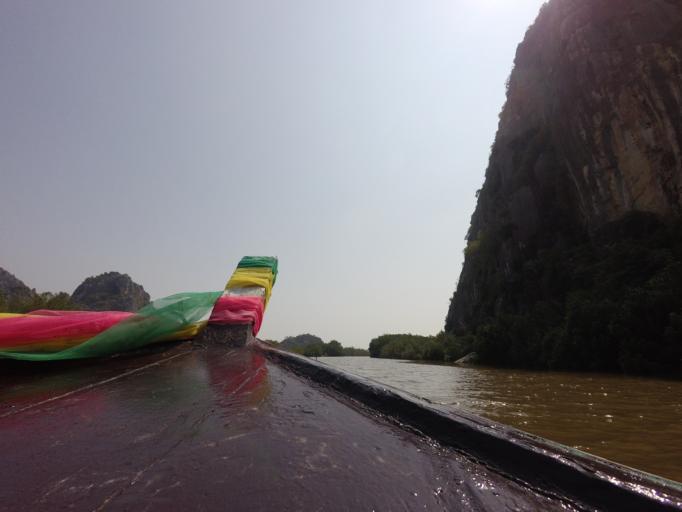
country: TH
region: Prachuap Khiri Khan
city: Kui Buri
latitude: 12.1420
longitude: 99.9551
